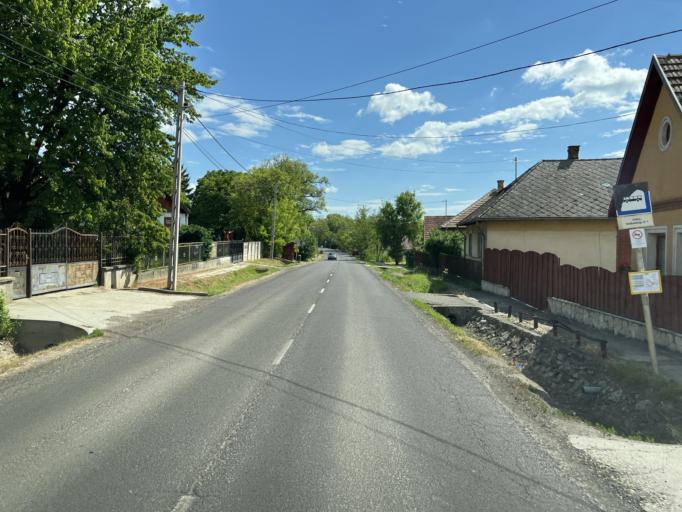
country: HU
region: Pest
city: Valko
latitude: 47.5666
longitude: 19.5198
